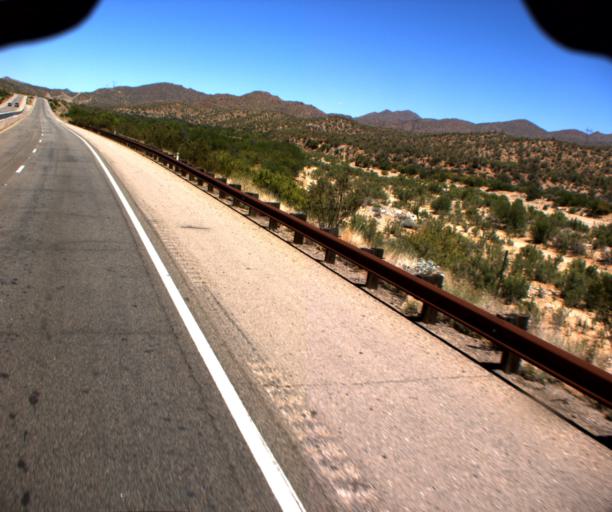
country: US
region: Arizona
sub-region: Yavapai County
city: Bagdad
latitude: 34.3801
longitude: -113.1938
